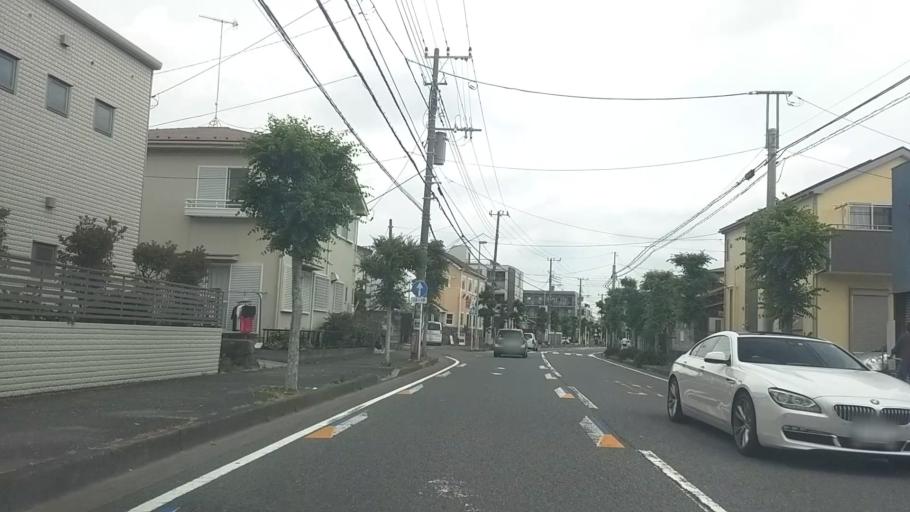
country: JP
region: Kanagawa
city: Fujisawa
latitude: 35.3279
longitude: 139.4679
